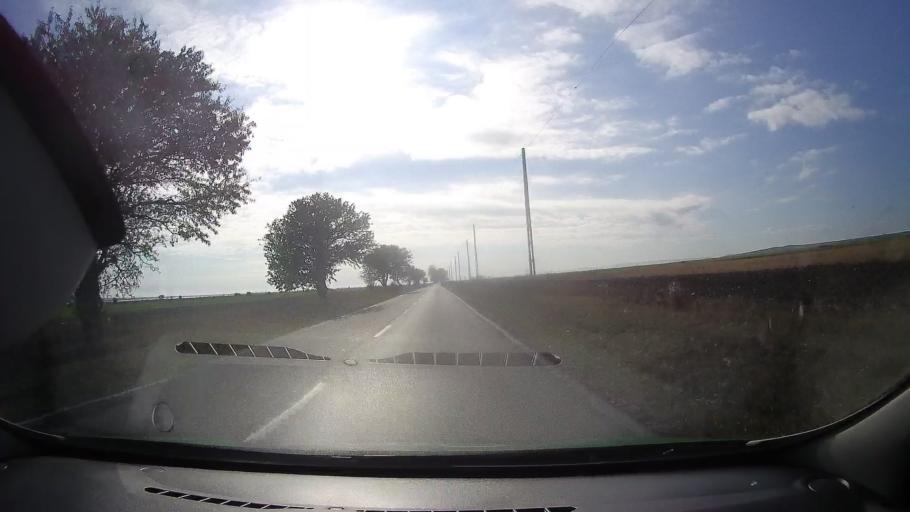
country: RO
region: Tulcea
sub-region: Comuna Valea Nucarilor
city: Agighiol
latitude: 45.0184
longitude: 28.8830
